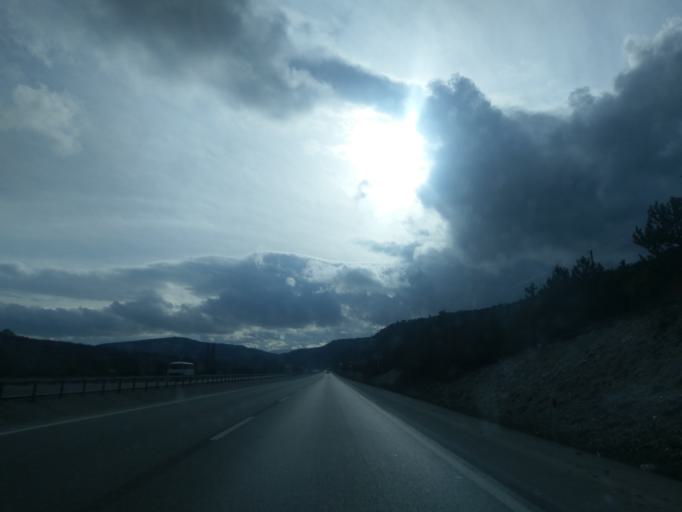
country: TR
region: Kuetahya
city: Sabuncu
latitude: 39.5473
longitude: 30.0588
